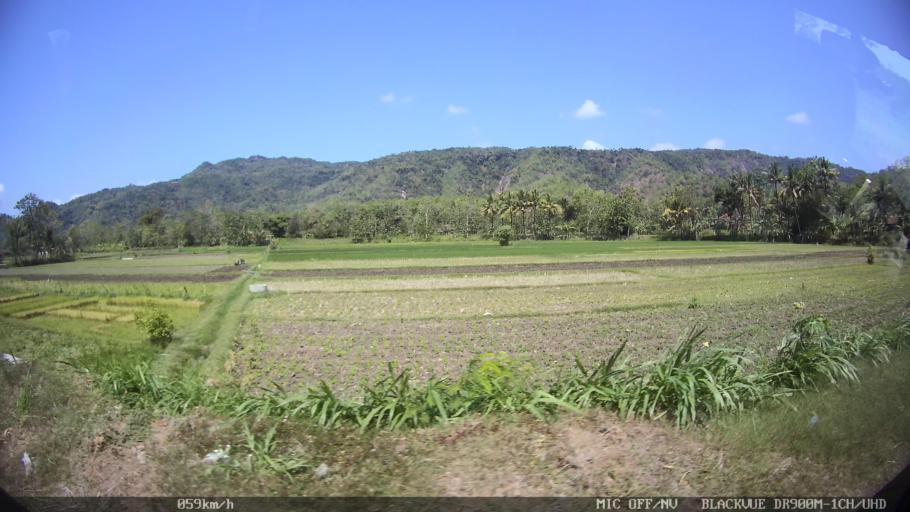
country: ID
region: Daerah Istimewa Yogyakarta
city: Pundong
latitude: -7.9713
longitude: 110.3502
